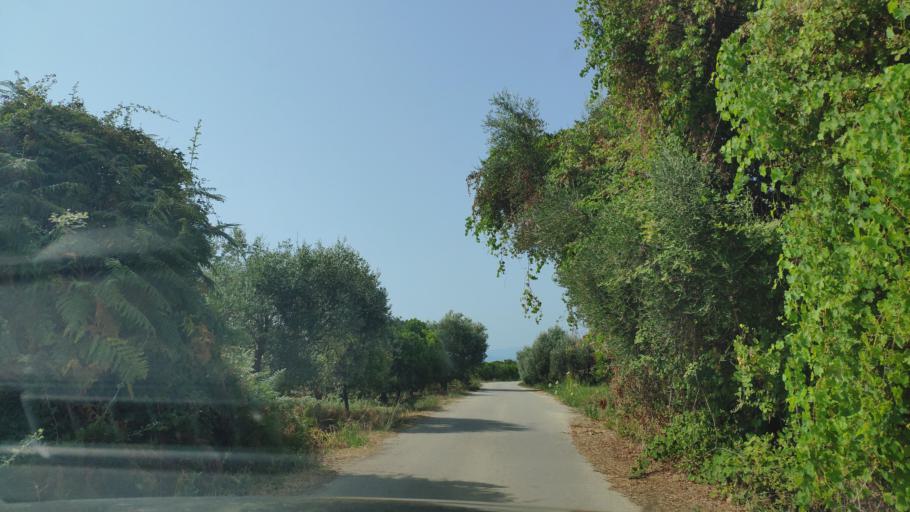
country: GR
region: Epirus
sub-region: Nomos Artas
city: Kompoti
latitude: 39.0641
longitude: 21.0760
